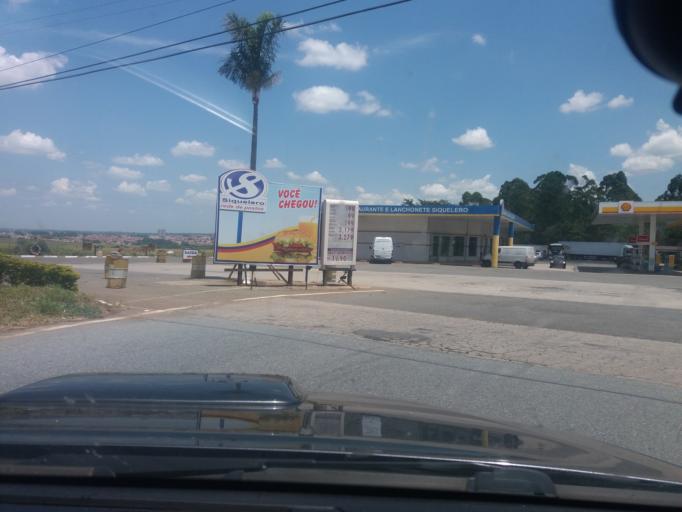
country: BR
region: Sao Paulo
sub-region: Itapetininga
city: Itapetininga
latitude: -23.5936
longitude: -47.9929
